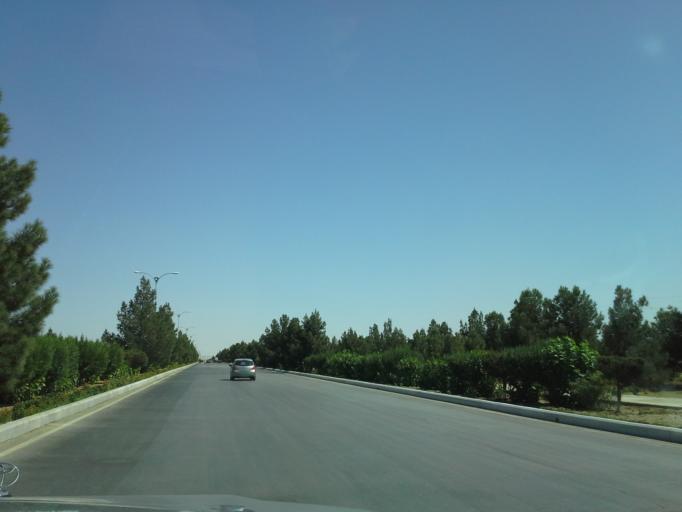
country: TM
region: Ahal
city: Annau
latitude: 37.9184
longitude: 58.4571
